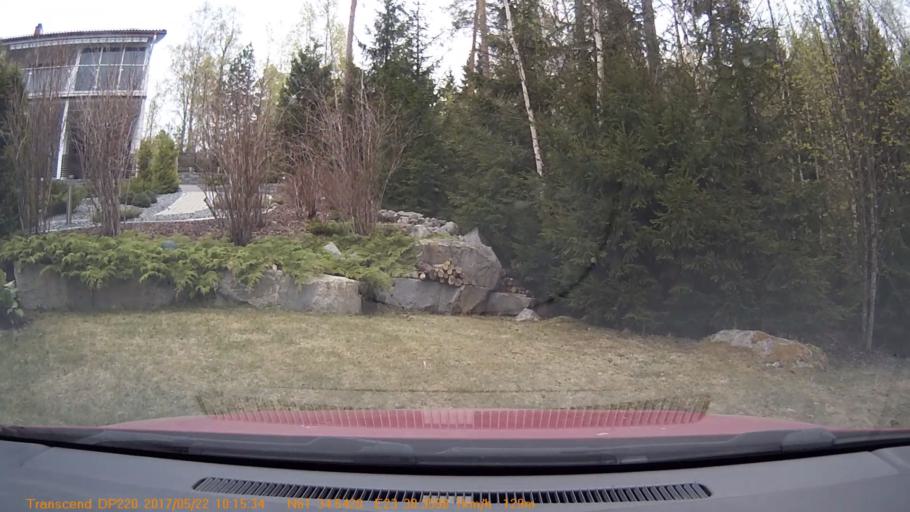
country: FI
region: Pirkanmaa
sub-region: Tampere
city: Yloejaervi
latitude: 61.5757
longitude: 23.6393
